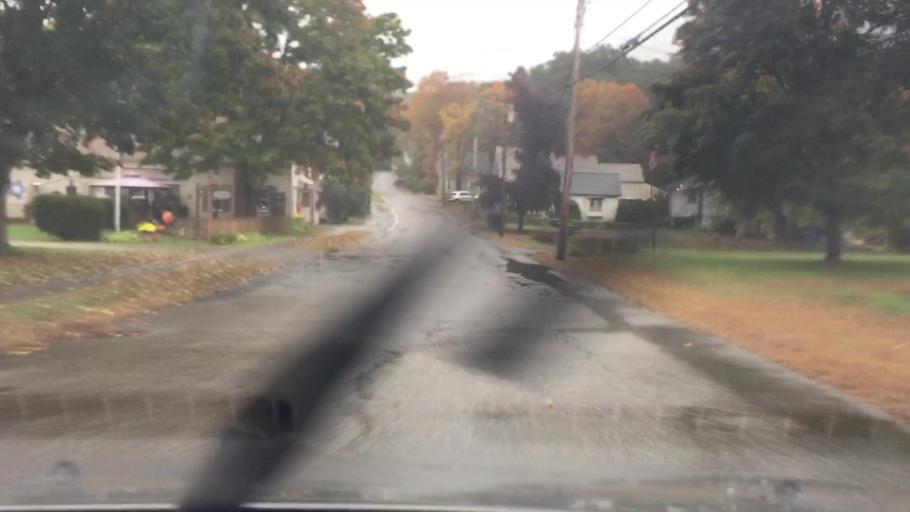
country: US
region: New Hampshire
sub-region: Cheshire County
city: Keene
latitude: 42.9446
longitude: -72.2714
